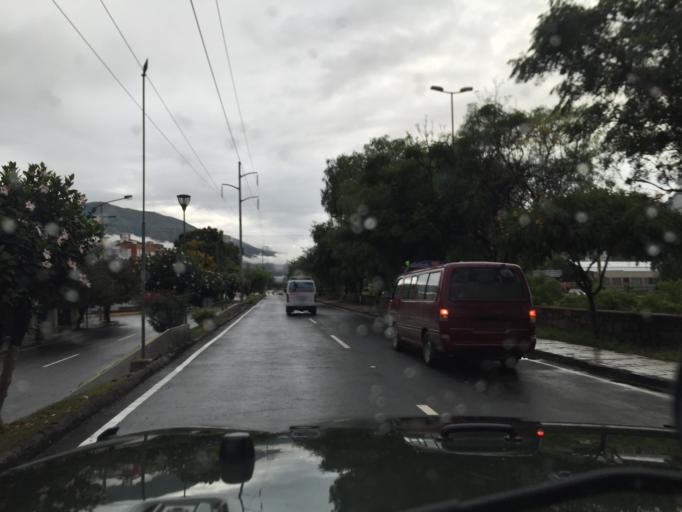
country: BO
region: Cochabamba
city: Cochabamba
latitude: -17.3799
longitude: -66.1549
